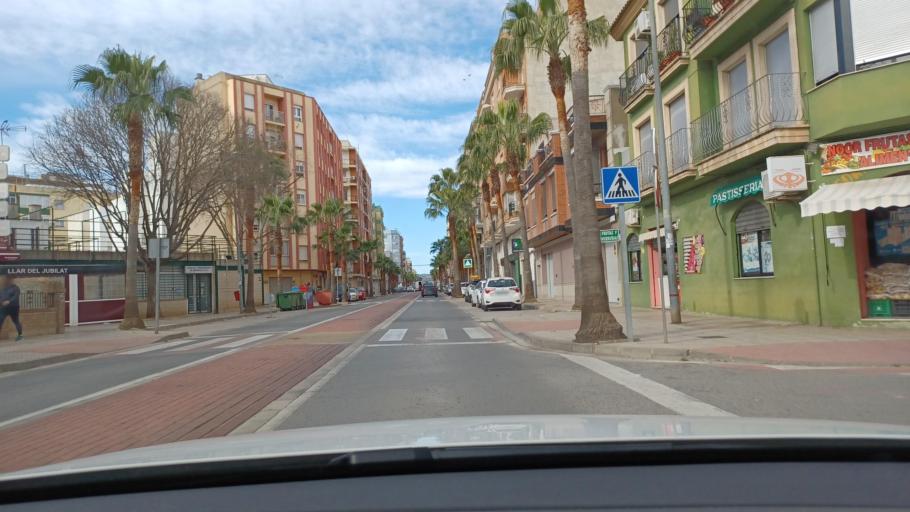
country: ES
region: Valencia
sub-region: Provincia de Valencia
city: Benifaio
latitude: 39.2884
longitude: -0.4216
